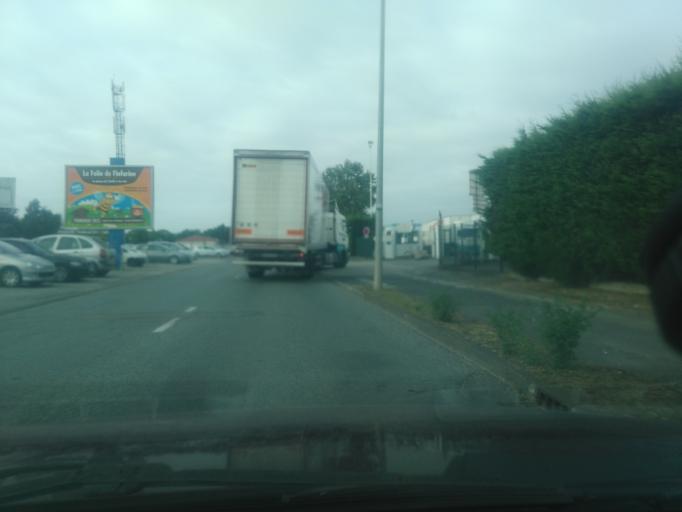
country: FR
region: Pays de la Loire
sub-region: Departement de la Vendee
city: La Roche-sur-Yon
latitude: 46.6869
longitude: -1.4331
